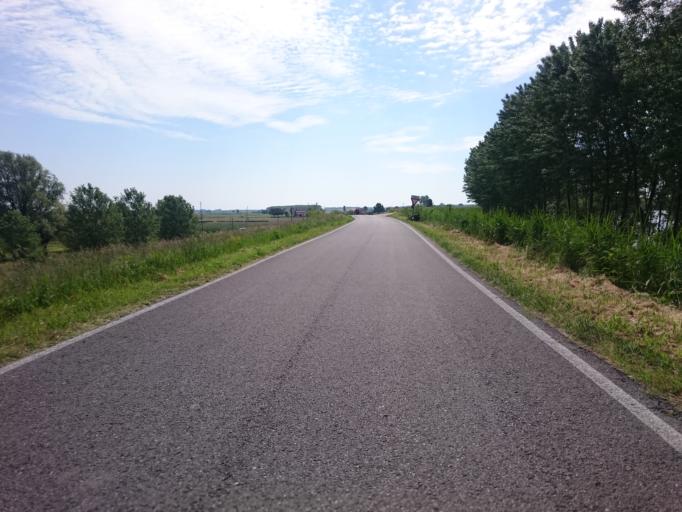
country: IT
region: Veneto
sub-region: Provincia di Rovigo
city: Ariano
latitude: 44.9618
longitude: 12.1122
